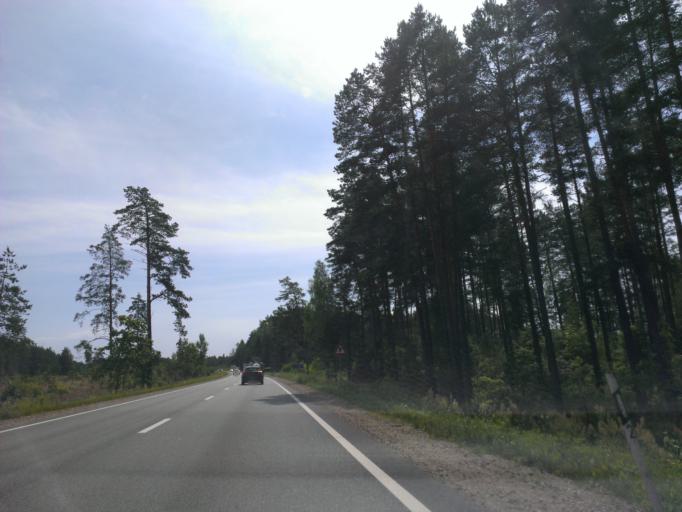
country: LV
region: Salaspils
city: Salaspils
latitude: 56.9267
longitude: 24.3907
